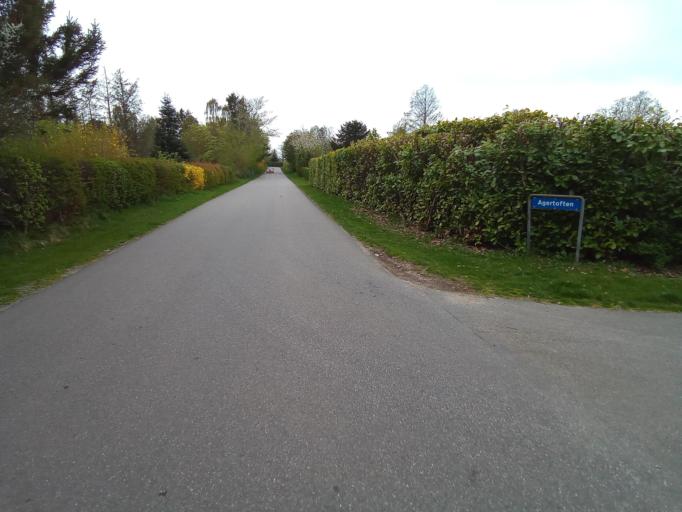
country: DK
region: Capital Region
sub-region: Frederikssund Kommune
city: Frederikssund
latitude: 55.8952
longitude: 12.0603
